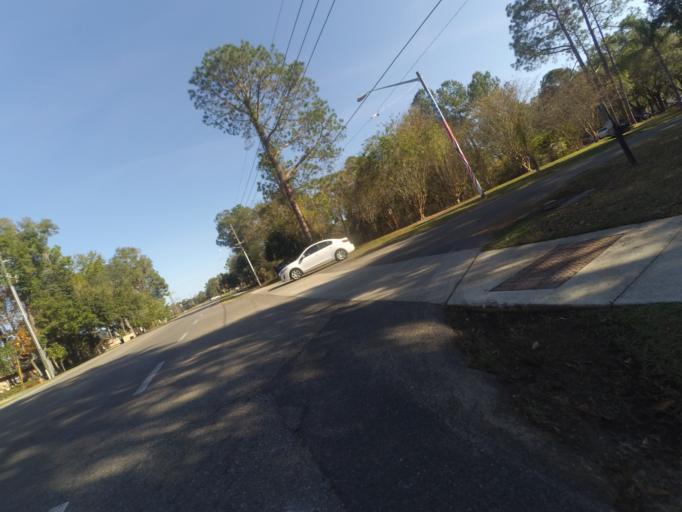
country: US
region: Florida
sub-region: Alachua County
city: Gainesville
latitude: 29.6201
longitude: -82.3578
